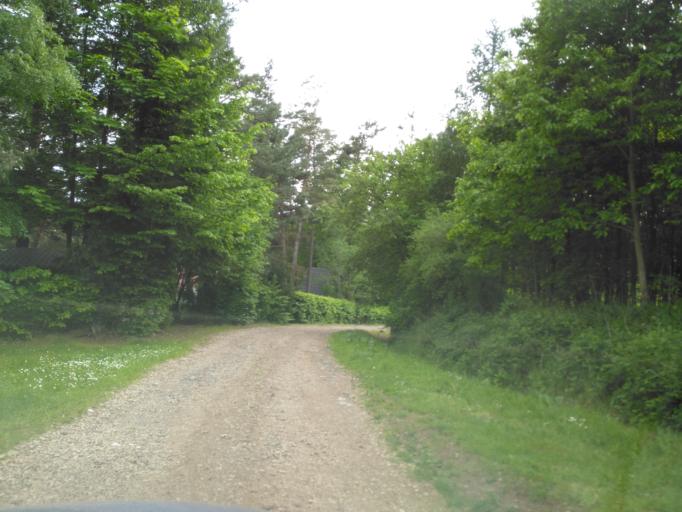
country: CZ
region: Plzensky
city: Zbiroh
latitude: 49.8587
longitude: 13.7285
